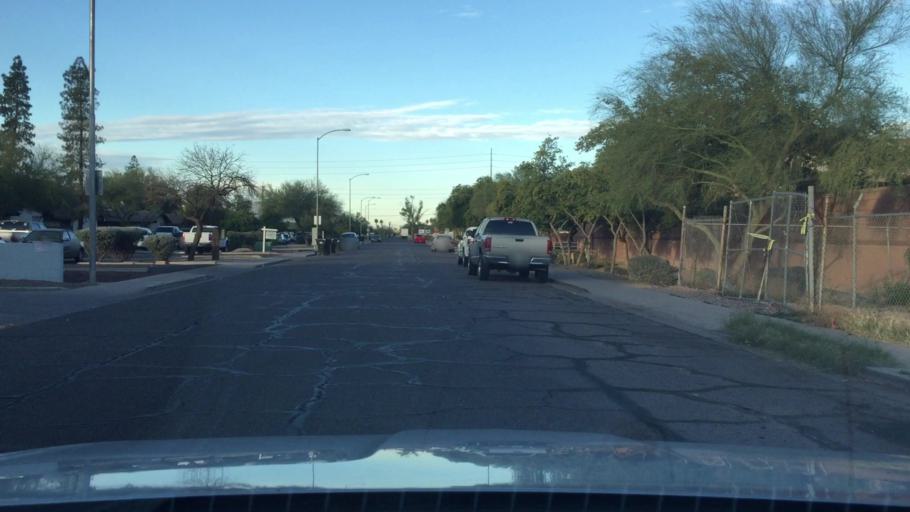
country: US
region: Arizona
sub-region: Maricopa County
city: Mesa
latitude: 33.4132
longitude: -111.8461
